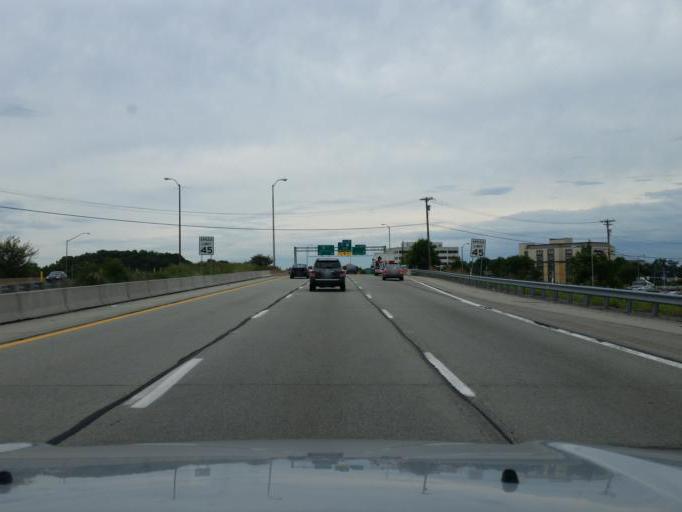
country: US
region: Pennsylvania
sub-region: Allegheny County
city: Monroeville
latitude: 40.4414
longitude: -79.7616
